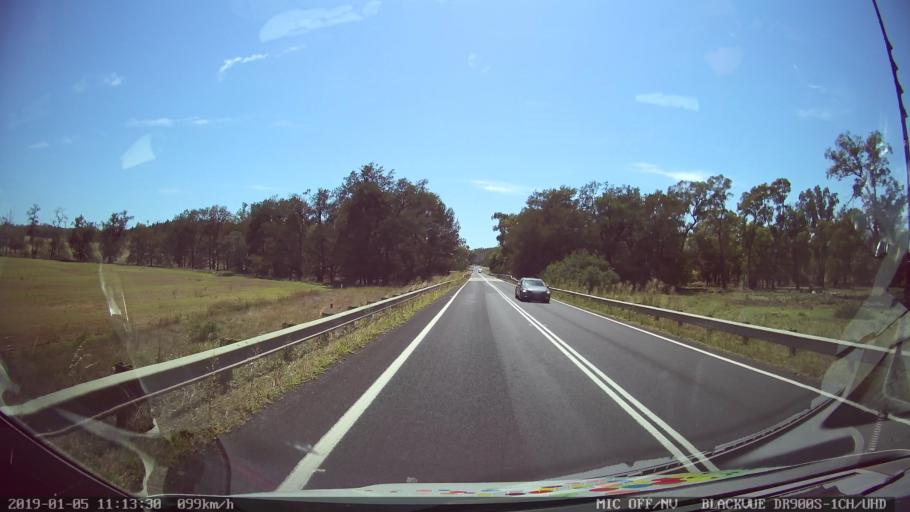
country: AU
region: New South Wales
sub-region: Warrumbungle Shire
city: Coonabarabran
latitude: -31.3702
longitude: 149.2716
